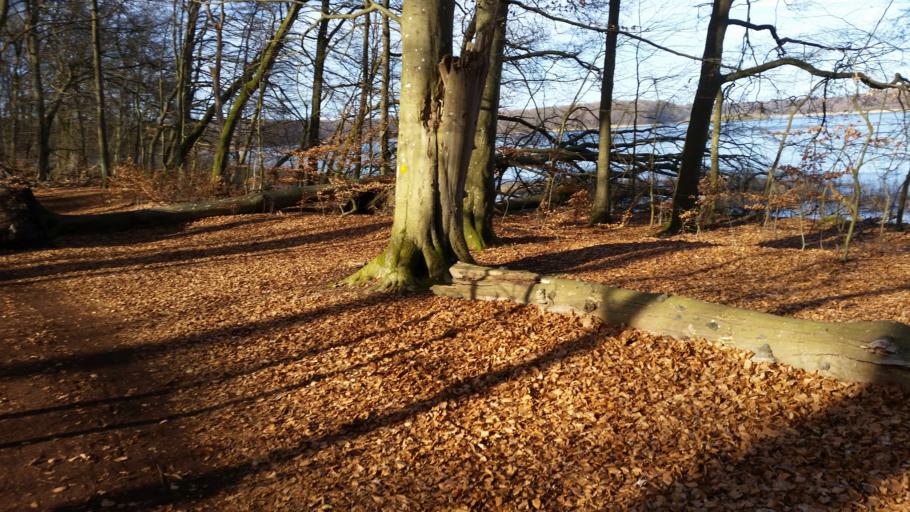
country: DK
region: Capital Region
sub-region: Helsingor Kommune
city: Hornbaek
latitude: 56.0257
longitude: 12.4795
